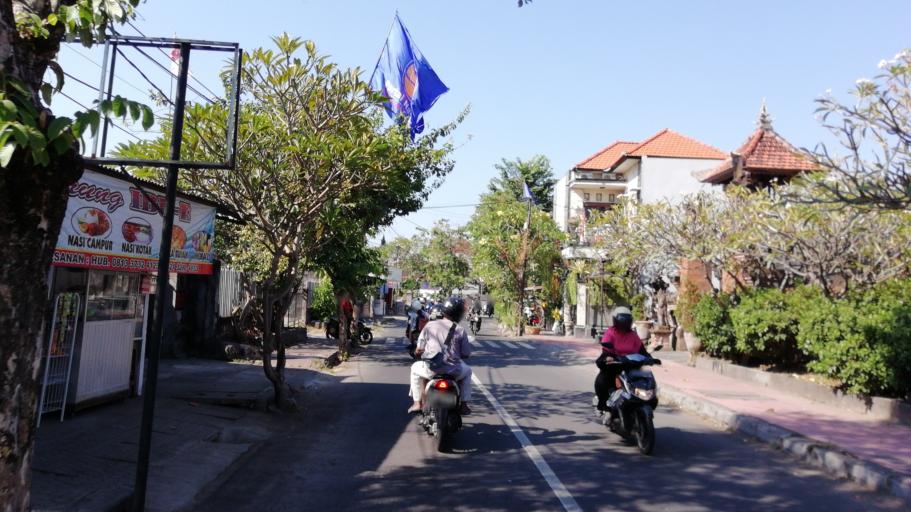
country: ID
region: Bali
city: Denpasar
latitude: -8.6642
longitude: 115.2229
